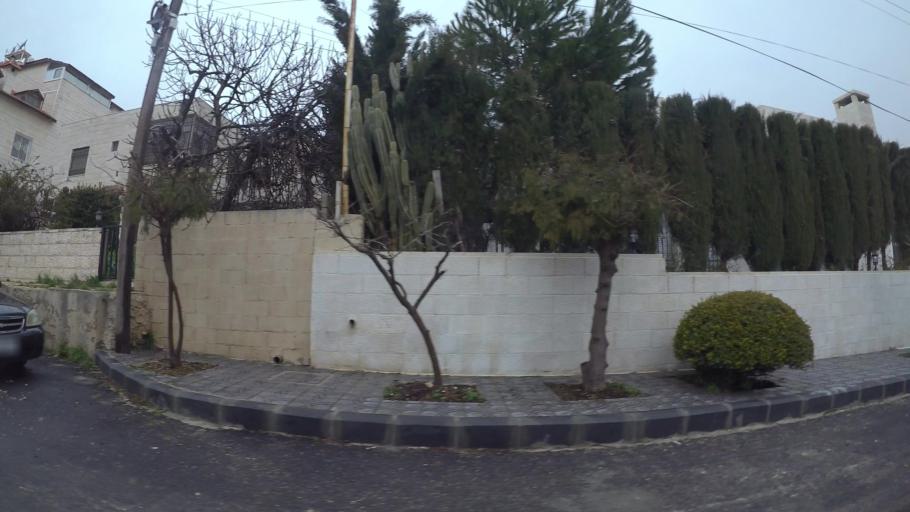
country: JO
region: Amman
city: Al Jubayhah
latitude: 32.0116
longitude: 35.8308
